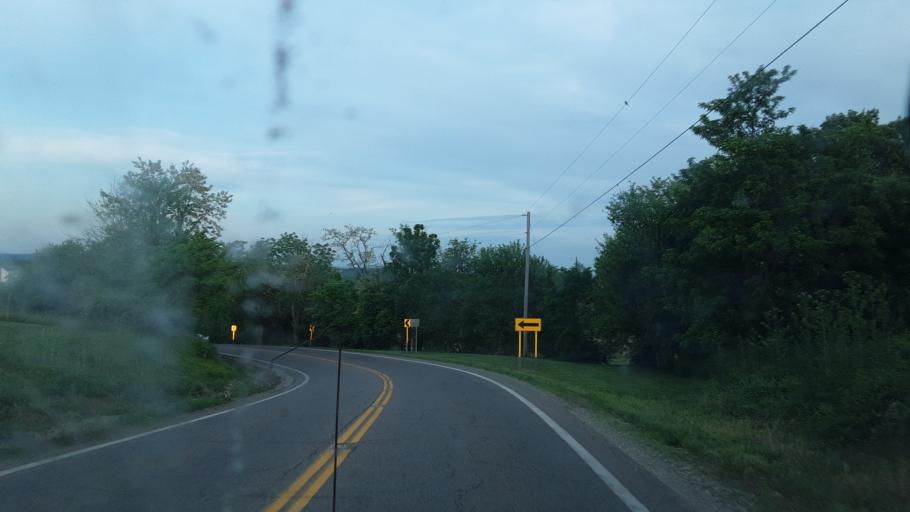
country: US
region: Ohio
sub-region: Ross County
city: Kingston
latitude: 39.4614
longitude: -82.7627
